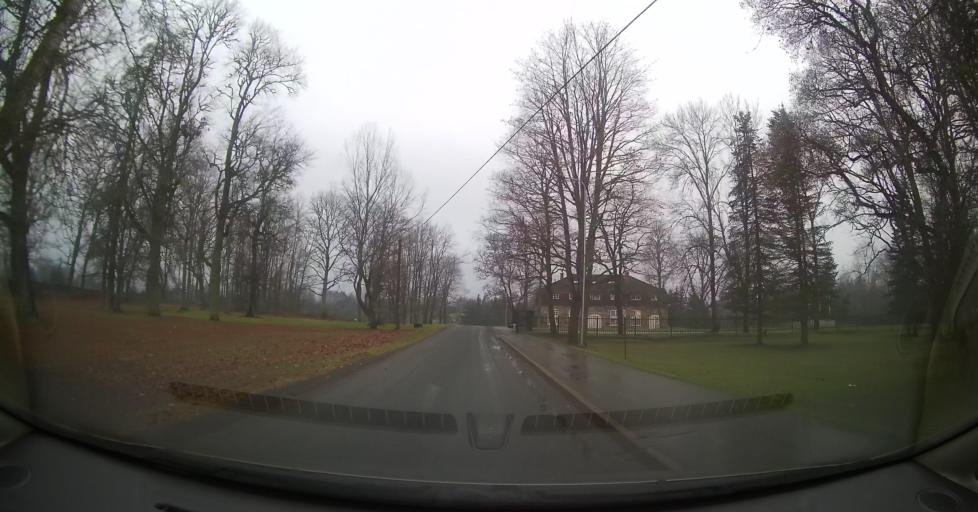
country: EE
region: Tartu
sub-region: Alatskivi vald
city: Kallaste
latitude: 58.3804
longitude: 27.0455
